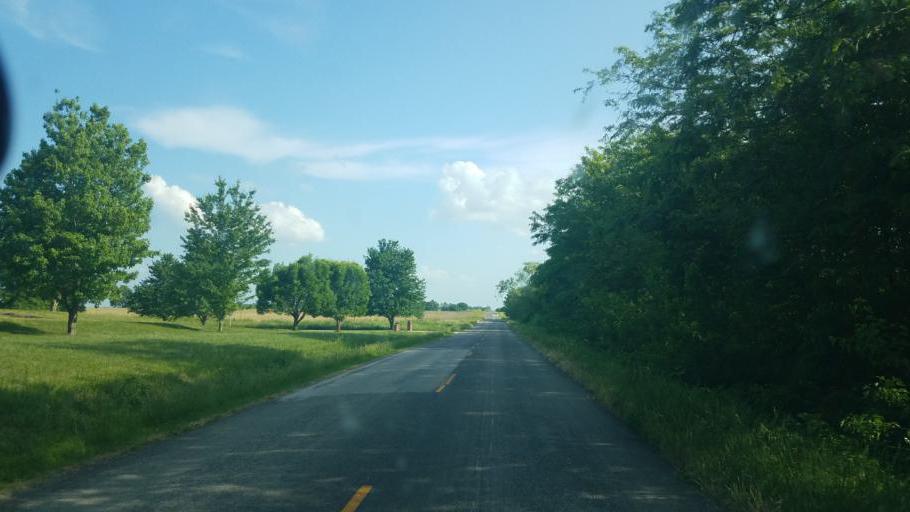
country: US
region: Missouri
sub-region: Moniteau County
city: California
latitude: 38.8043
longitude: -92.6048
